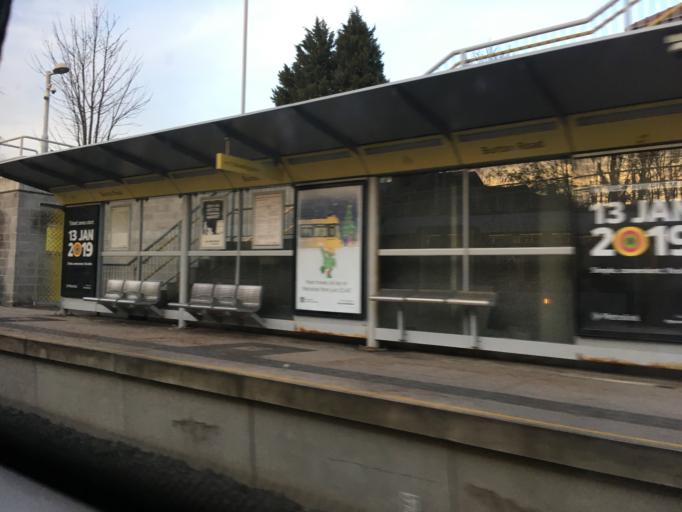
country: GB
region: England
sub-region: Manchester
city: Didsbury
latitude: 53.4289
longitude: -2.2403
